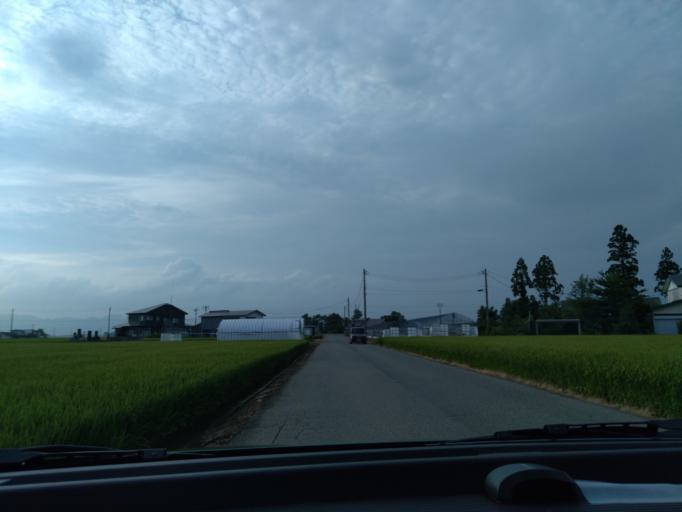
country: JP
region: Akita
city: Omagari
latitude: 39.4067
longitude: 140.5138
